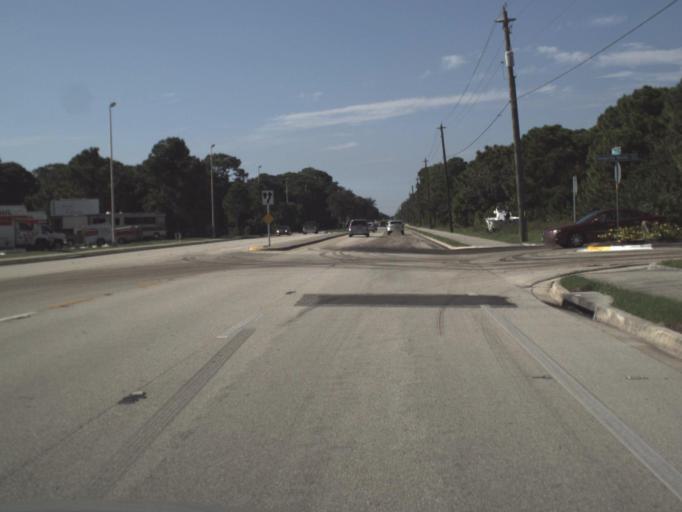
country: US
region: Florida
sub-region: Sarasota County
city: Englewood
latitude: 26.9768
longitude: -82.3560
